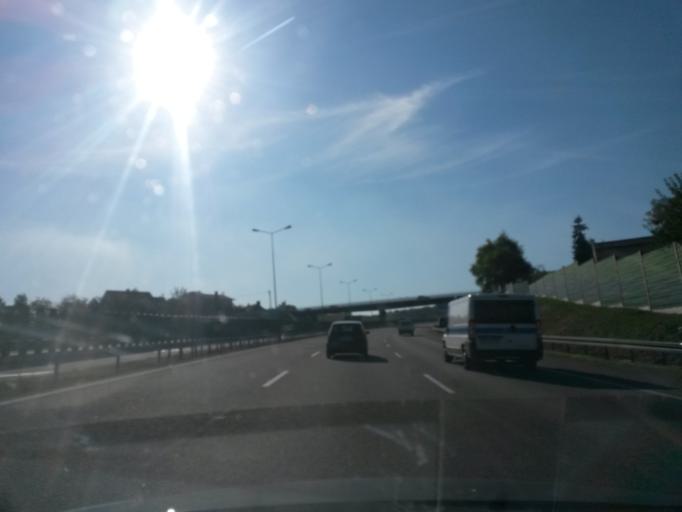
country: PL
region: Opole Voivodeship
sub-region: Powiat strzelecki
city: Lesnica
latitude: 50.4634
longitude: 18.1682
